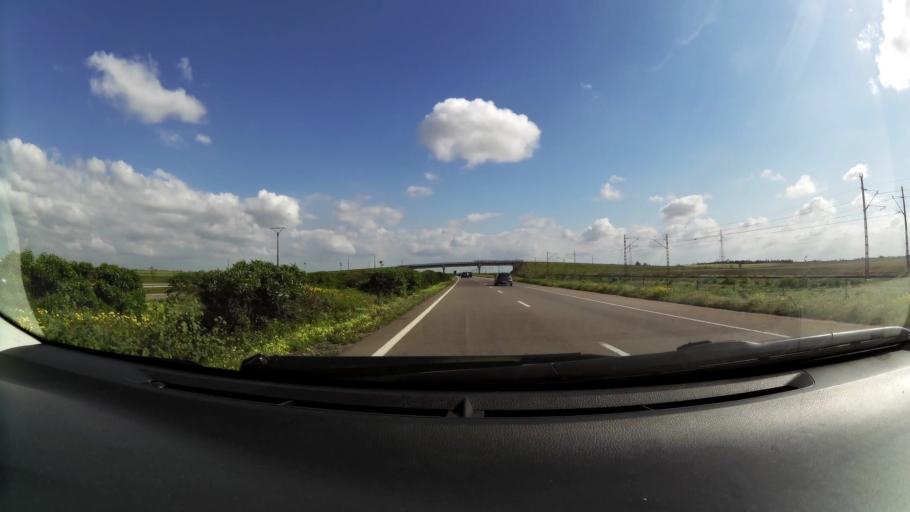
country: MA
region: Chaouia-Ouardigha
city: Nouaseur
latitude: 33.3581
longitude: -7.6186
